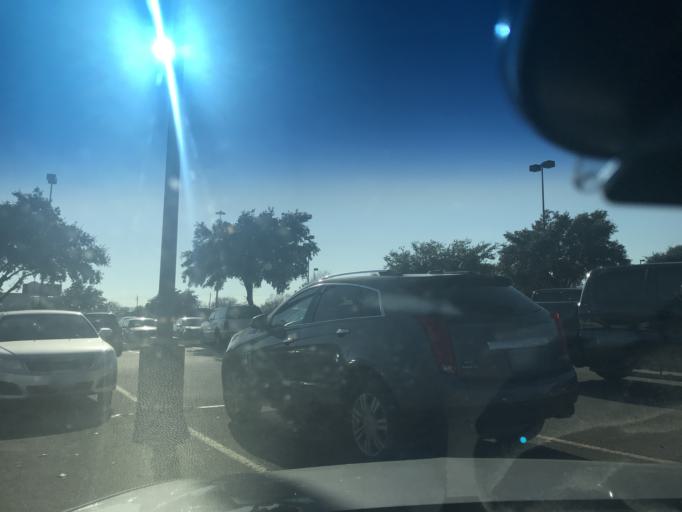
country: US
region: Texas
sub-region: Travis County
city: Wells Branch
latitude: 30.4210
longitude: -97.6704
